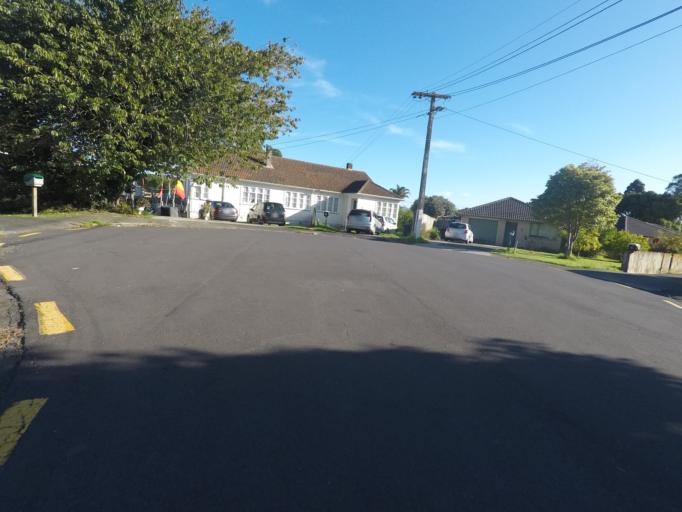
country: NZ
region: Auckland
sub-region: Auckland
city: Rosebank
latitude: -36.8972
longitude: 174.7125
